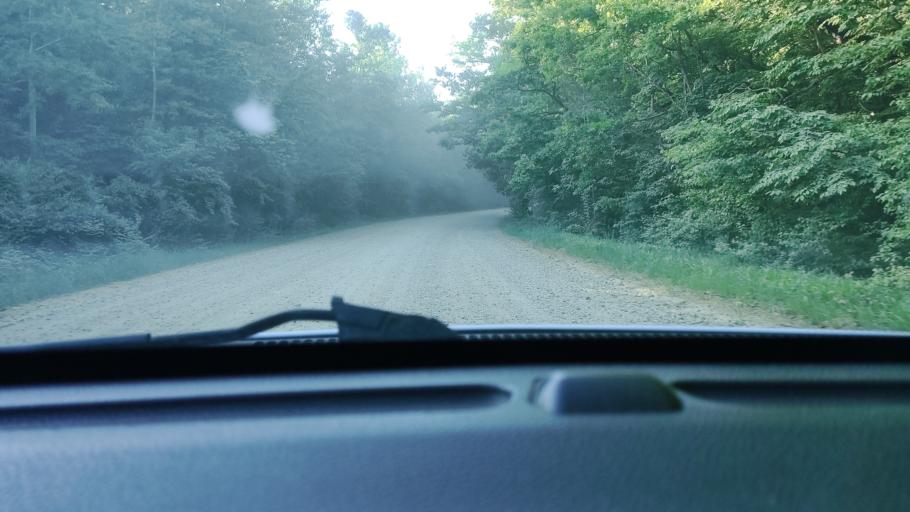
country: RU
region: Krasnodarskiy
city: Goryachiy Klyuch
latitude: 44.7130
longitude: 38.9913
